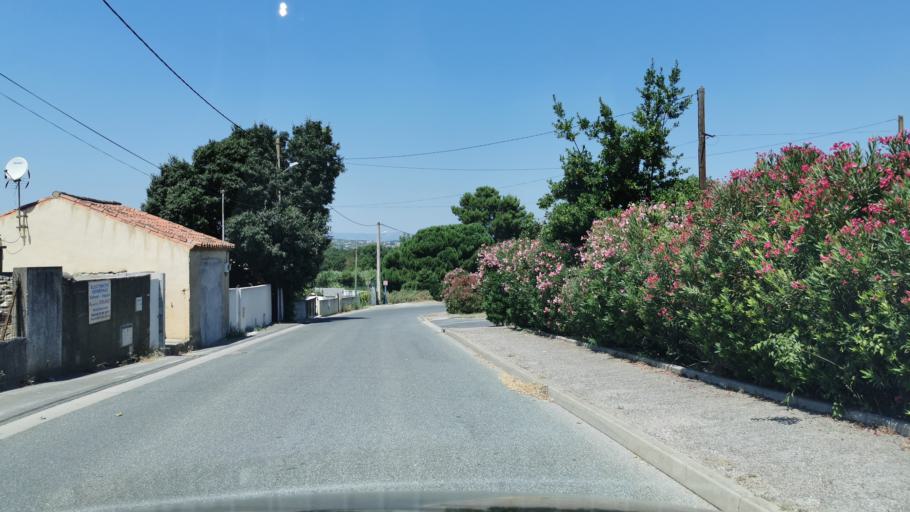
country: FR
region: Languedoc-Roussillon
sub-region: Departement de l'Herault
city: Maureilhan
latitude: 43.3602
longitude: 3.1184
